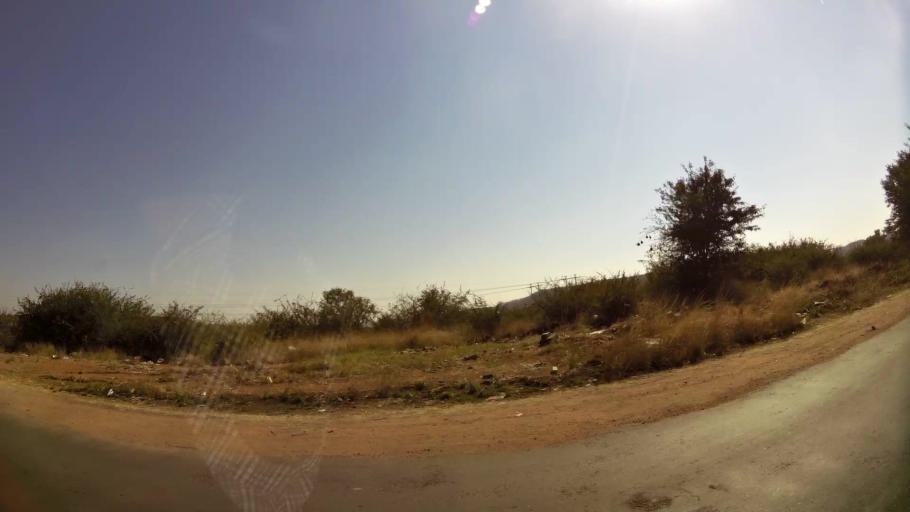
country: ZA
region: Gauteng
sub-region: City of Tshwane Metropolitan Municipality
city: Mabopane
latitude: -25.5401
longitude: 28.0806
